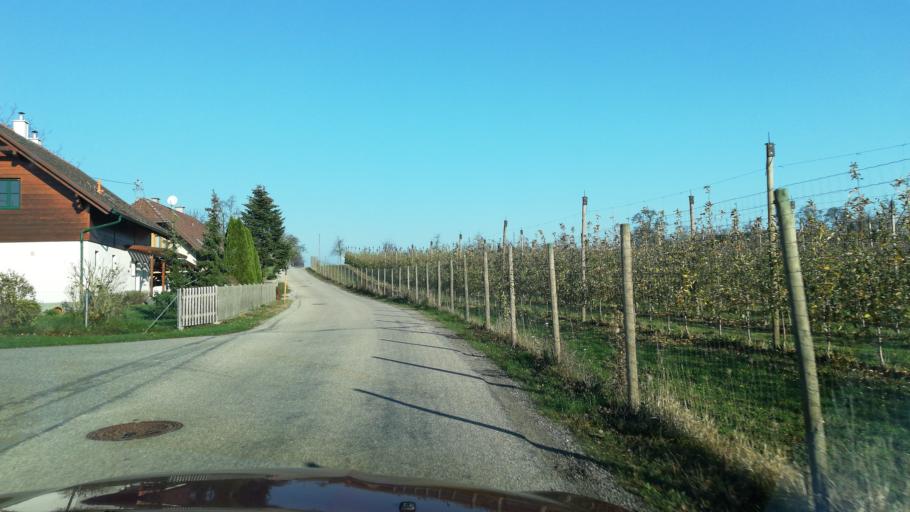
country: AT
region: Upper Austria
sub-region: Wels-Land
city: Buchkirchen
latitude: 48.2630
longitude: 14.0130
